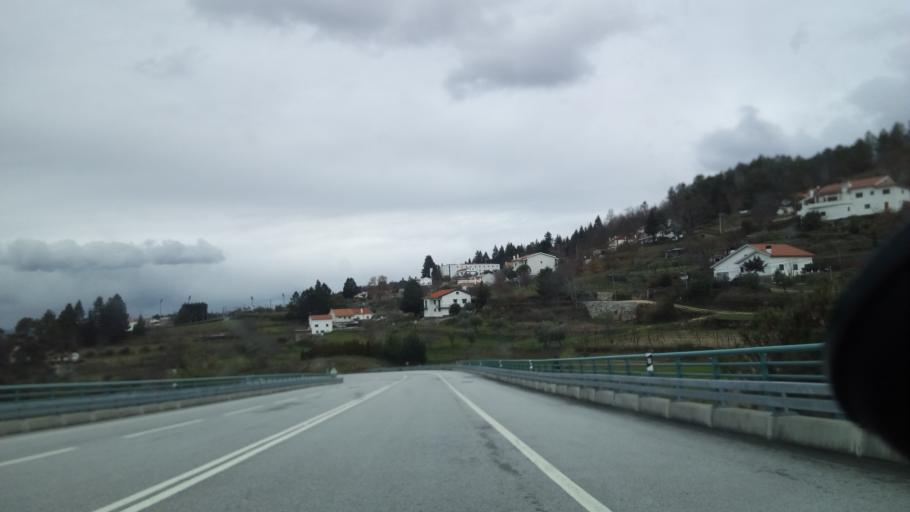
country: PT
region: Guarda
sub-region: Manteigas
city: Manteigas
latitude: 40.4800
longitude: -7.5977
